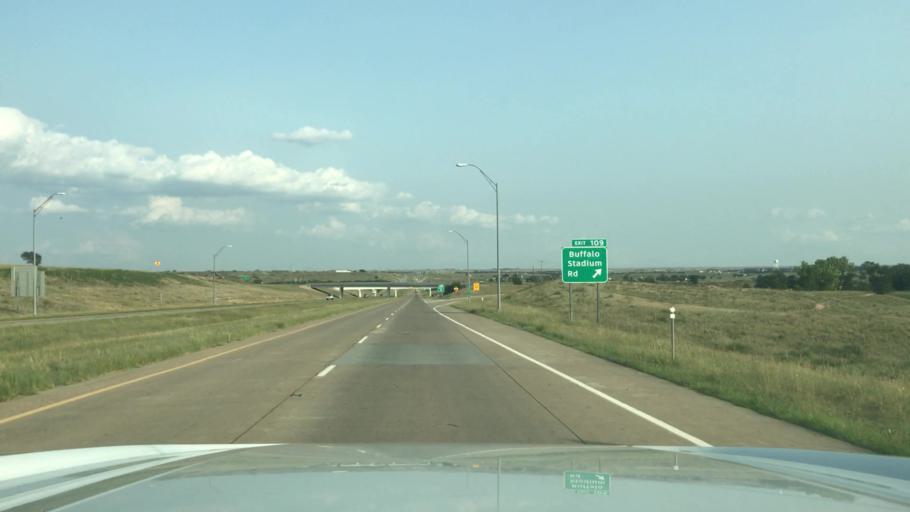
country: US
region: Texas
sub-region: Randall County
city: Canyon
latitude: 35.0173
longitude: -101.9143
